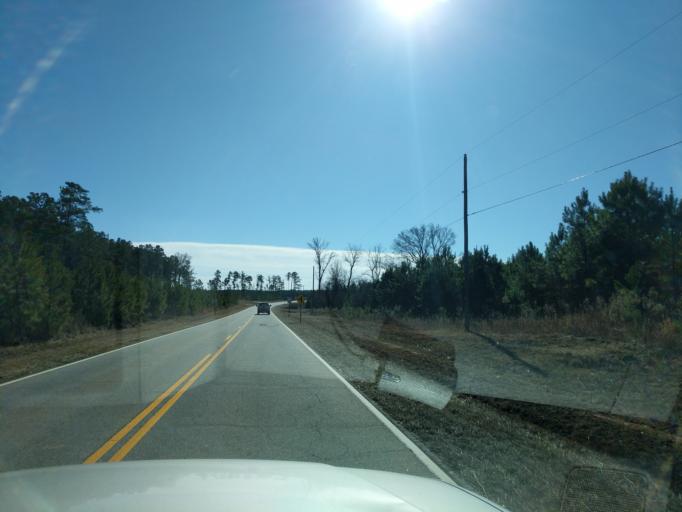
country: US
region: South Carolina
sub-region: Saluda County
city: Saluda
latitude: 34.1137
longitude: -81.8325
